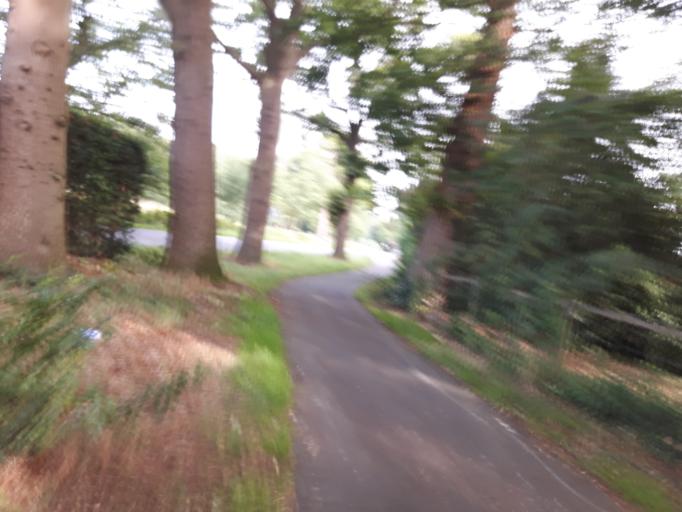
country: DE
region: Lower Saxony
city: Delmenhorst
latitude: 53.0915
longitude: 8.6038
